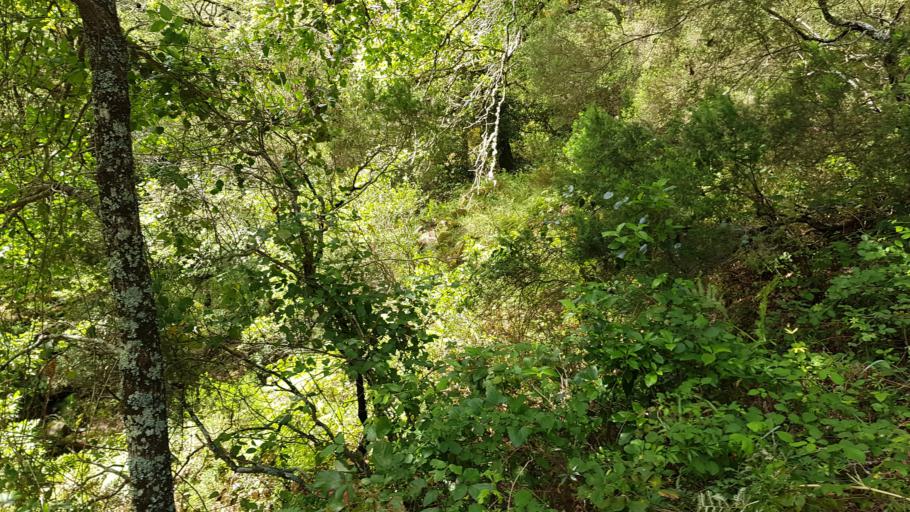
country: ES
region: Andalusia
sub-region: Provincia de Cadiz
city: Alcala de los Gazules
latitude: 36.5165
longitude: -5.5966
